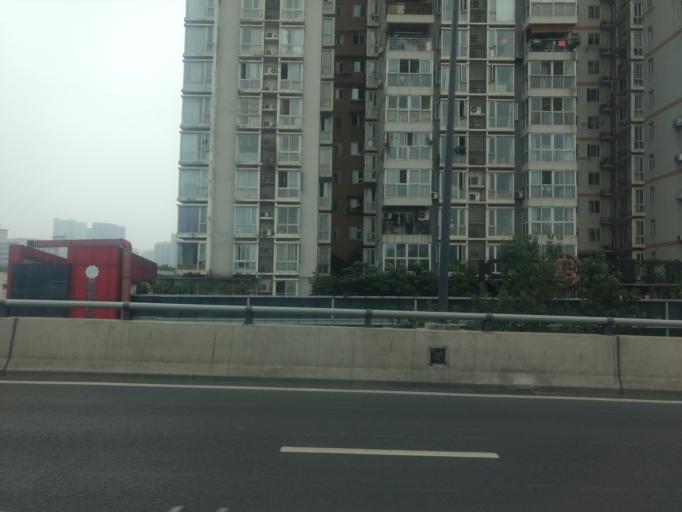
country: CN
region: Sichuan
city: Chengdu
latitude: 30.6785
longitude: 104.0920
